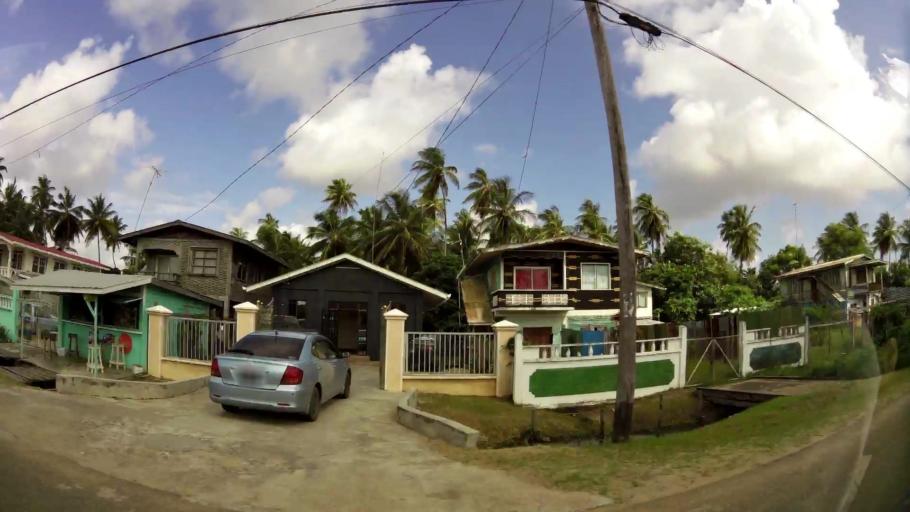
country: GY
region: Demerara-Mahaica
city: Mahaica Village
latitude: 6.7099
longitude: -57.9273
